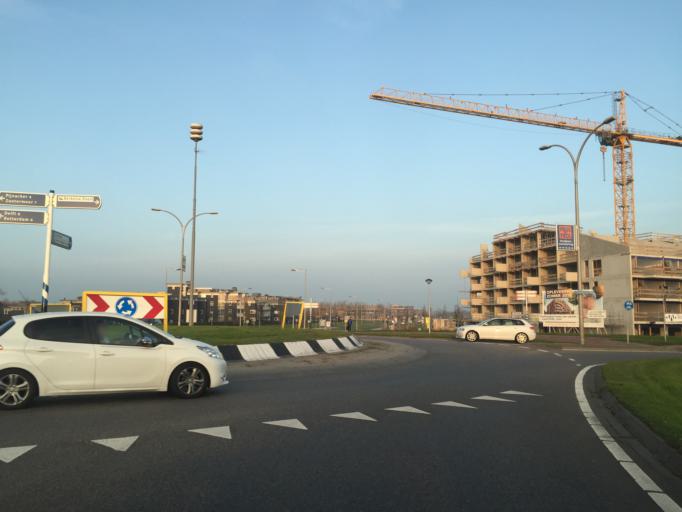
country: NL
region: South Holland
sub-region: Gemeente Lansingerland
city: Berkel en Rodenrijs
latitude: 51.9929
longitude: 4.4652
